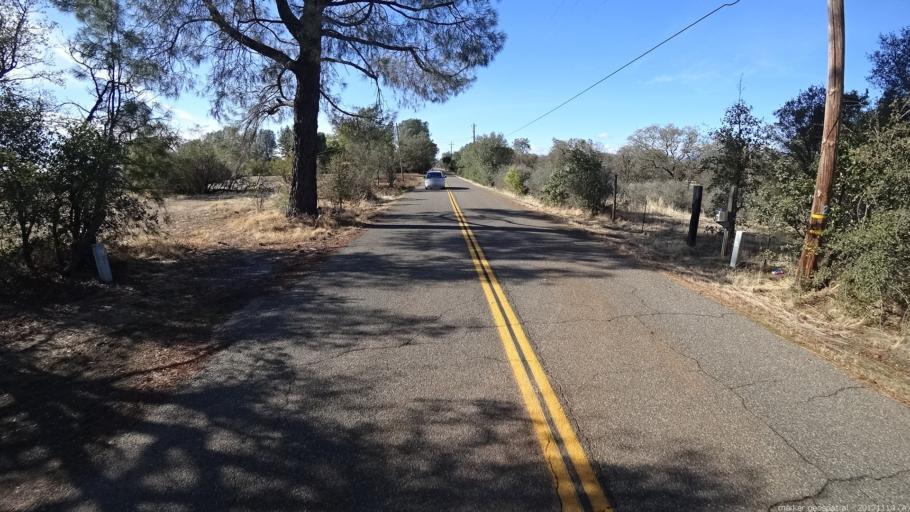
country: US
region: California
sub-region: Shasta County
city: Anderson
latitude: 40.4321
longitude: -122.4099
